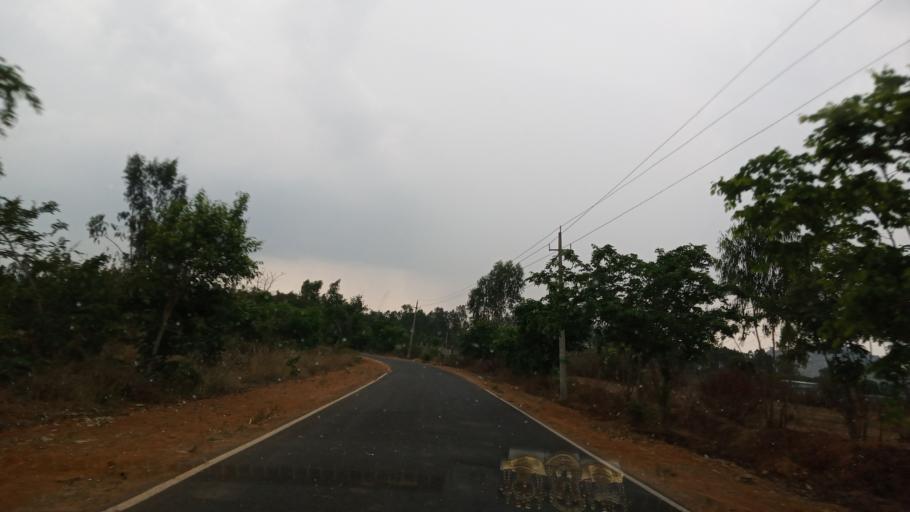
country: IN
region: Karnataka
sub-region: Kolar
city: Mulbagal
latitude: 13.1228
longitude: 78.3469
